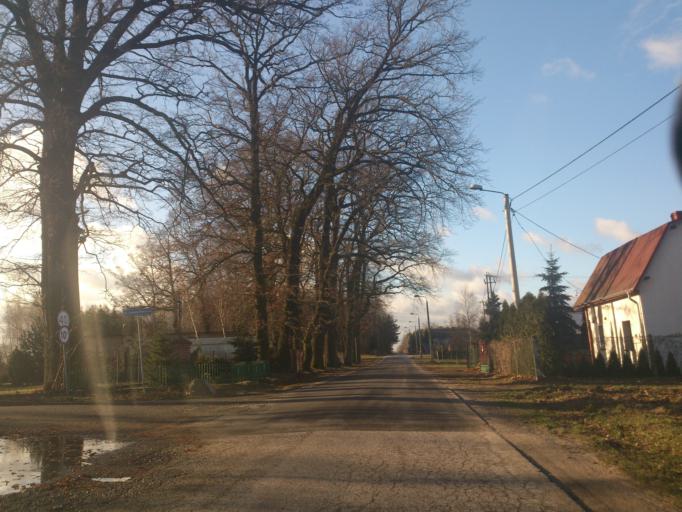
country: PL
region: Kujawsko-Pomorskie
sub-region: Powiat torunski
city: Lubicz Gorny
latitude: 53.0394
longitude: 18.8075
